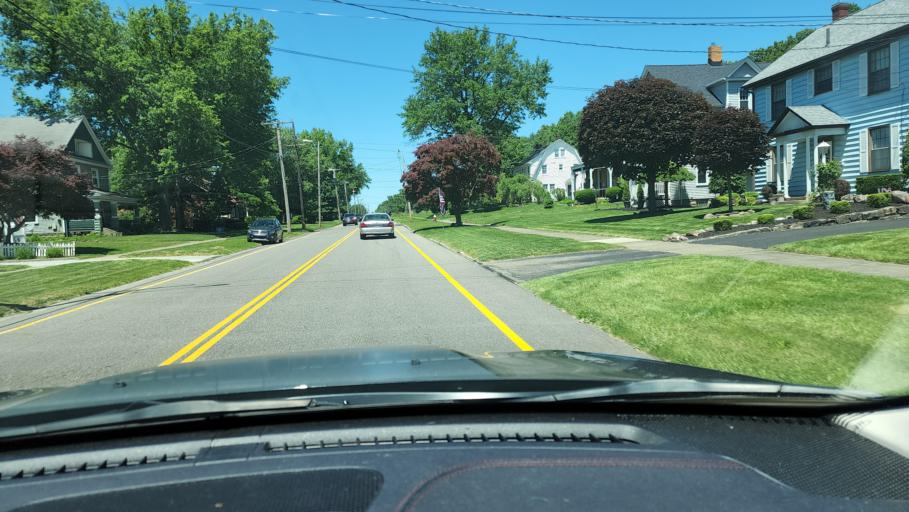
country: US
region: Ohio
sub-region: Trumbull County
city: Niles
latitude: 41.1850
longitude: -80.7449
